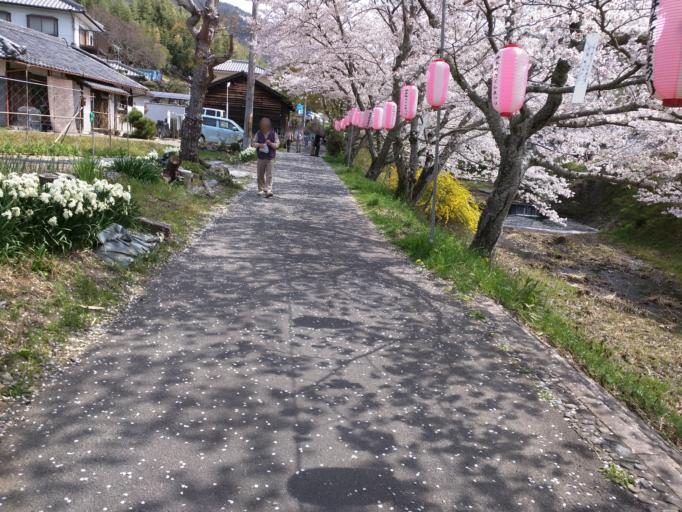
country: JP
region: Kyoto
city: Tanabe
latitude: 34.7986
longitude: 135.8130
